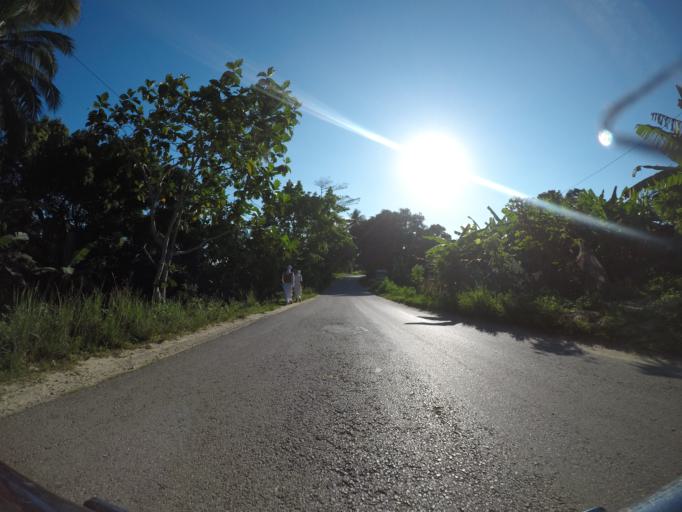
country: TZ
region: Pemba South
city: Chake Chake
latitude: -5.2992
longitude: 39.7564
